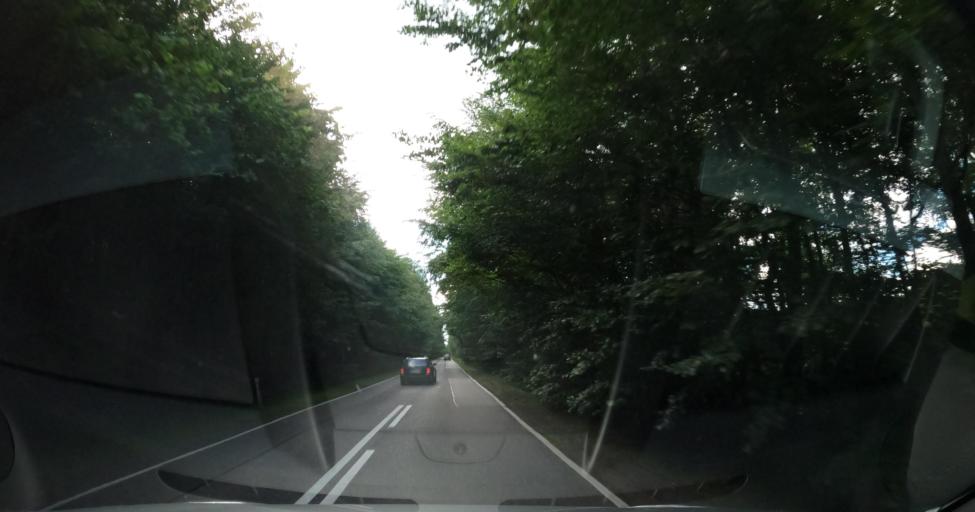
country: PL
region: Pomeranian Voivodeship
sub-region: Powiat bytowski
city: Czarna Dabrowka
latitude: 54.3773
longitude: 17.4938
